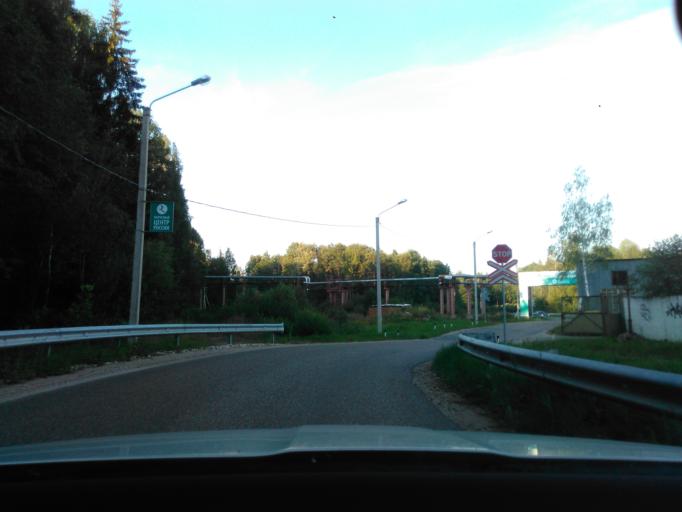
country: RU
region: Tverskaya
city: Konakovo
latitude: 56.7495
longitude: 36.7666
